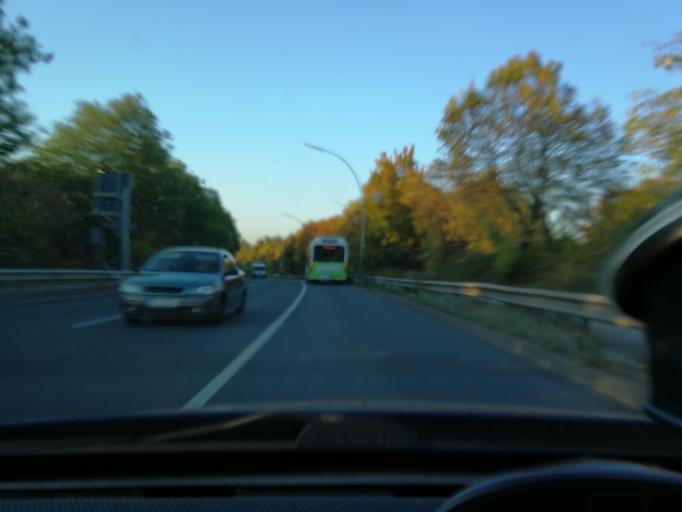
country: DE
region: Hamburg
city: Harburg
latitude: 53.4725
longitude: 9.9014
